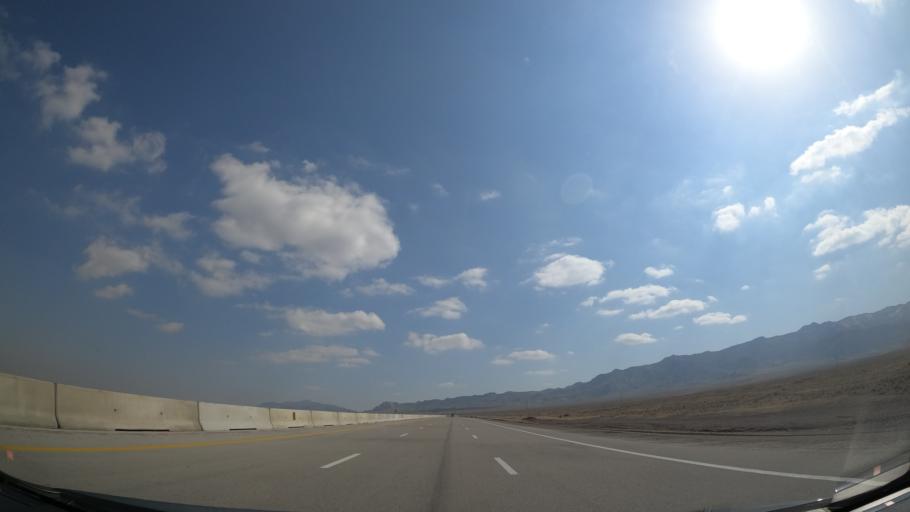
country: IR
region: Alborz
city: Eshtehard
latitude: 35.7232
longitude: 50.5669
